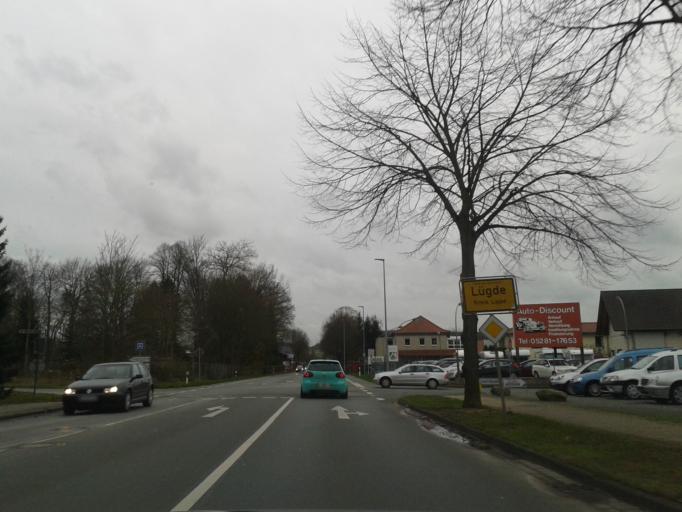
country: DE
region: Lower Saxony
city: Bad Pyrmont
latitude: 51.9722
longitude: 9.2665
